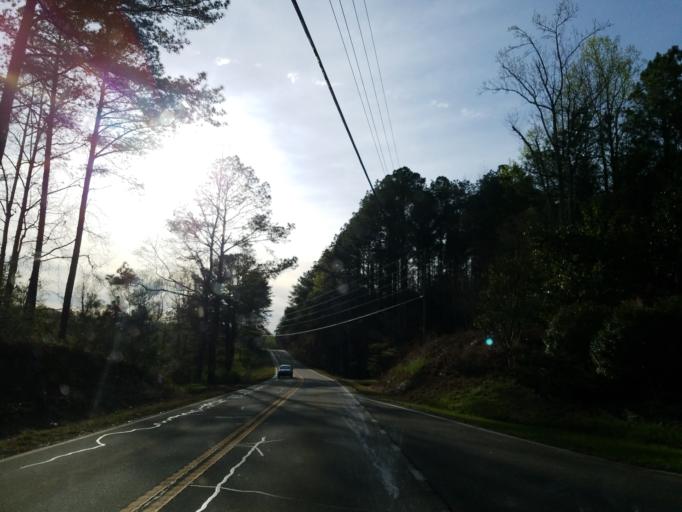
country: US
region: Georgia
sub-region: Pickens County
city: Jasper
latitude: 34.5127
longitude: -84.4488
